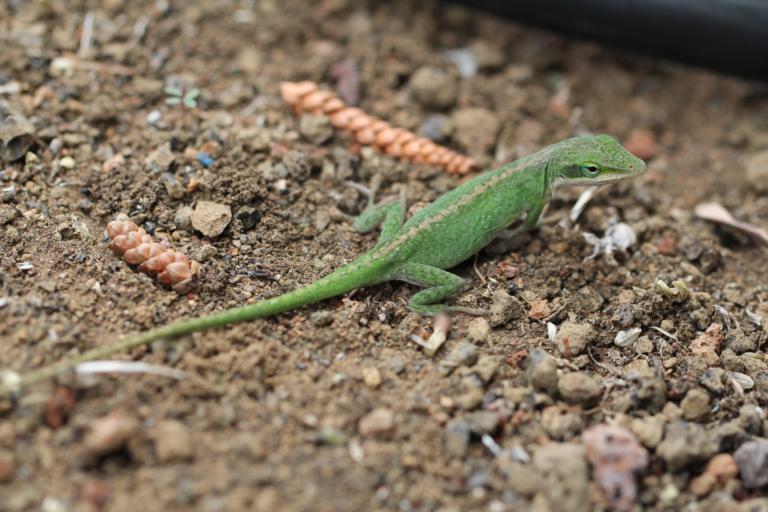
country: US
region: Hawaii
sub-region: Hawaii County
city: Waikoloa
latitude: 19.9257
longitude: -155.7947
